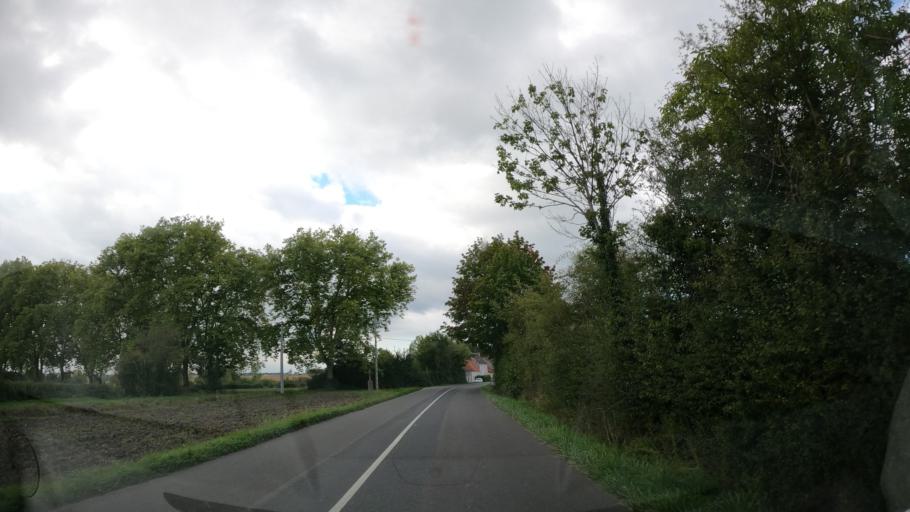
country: FR
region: Auvergne
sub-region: Departement de l'Allier
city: Lapalisse
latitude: 46.3703
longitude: 3.6123
